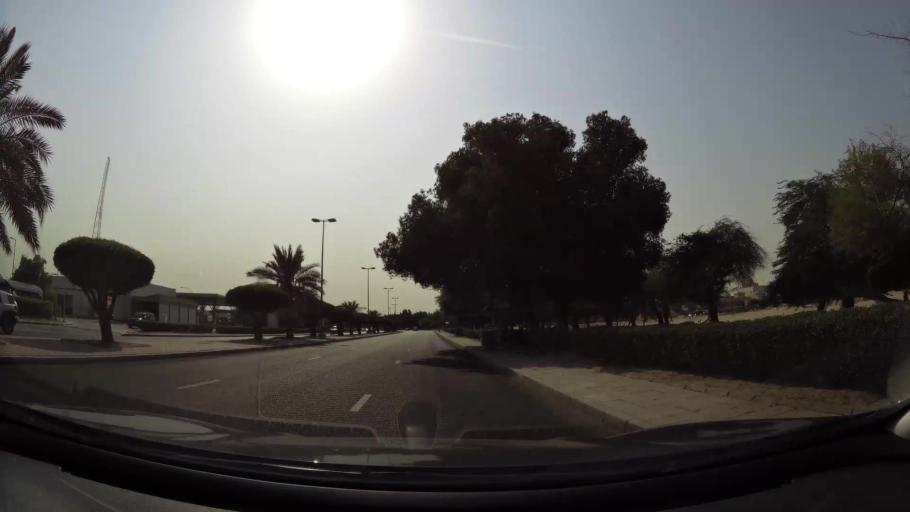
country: KW
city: Bayan
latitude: 29.3004
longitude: 48.0543
